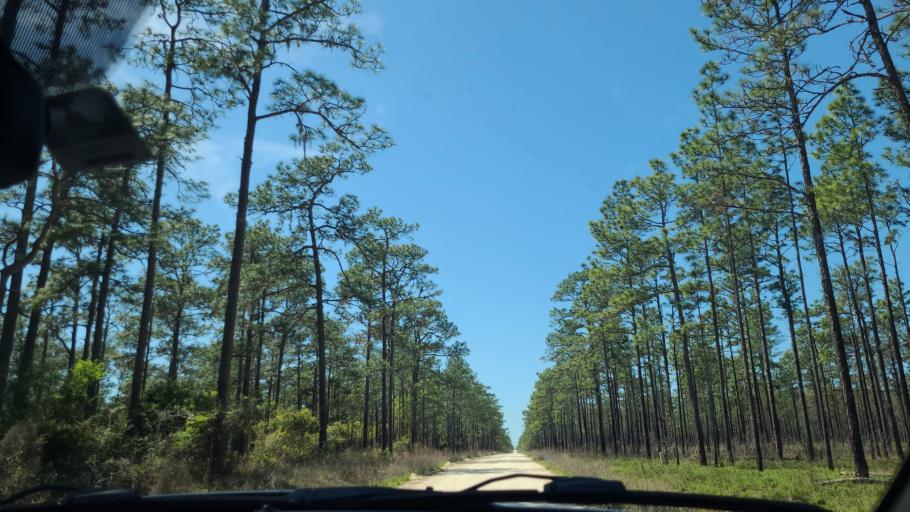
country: US
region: Florida
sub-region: Putnam County
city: Interlachen
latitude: 29.4289
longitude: -81.7921
